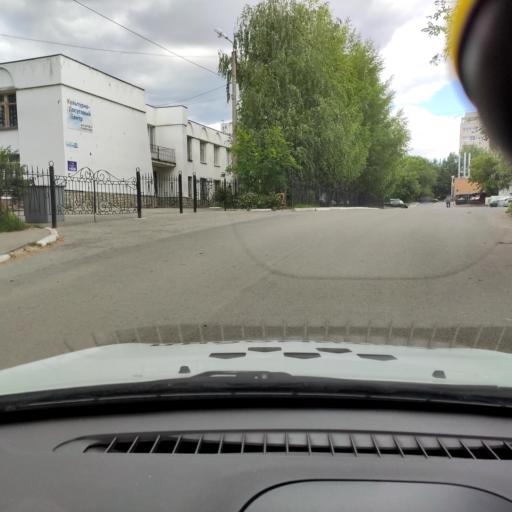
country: RU
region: Samara
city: Zhigulevsk
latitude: 53.4015
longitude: 49.5116
